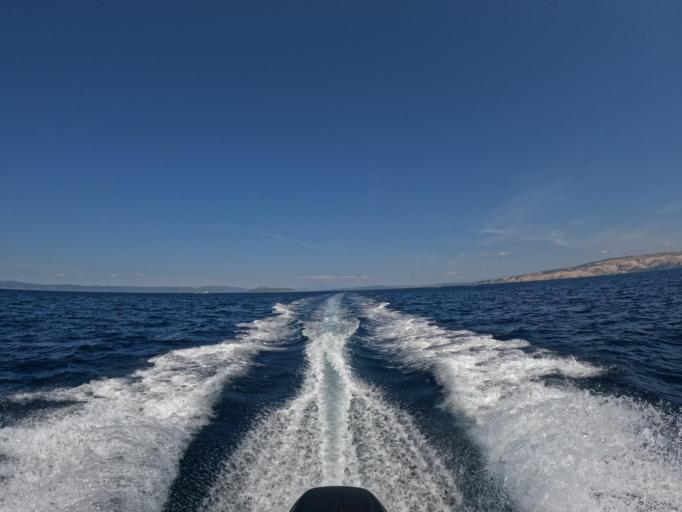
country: HR
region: Primorsko-Goranska
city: Lopar
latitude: 44.8957
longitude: 14.6402
